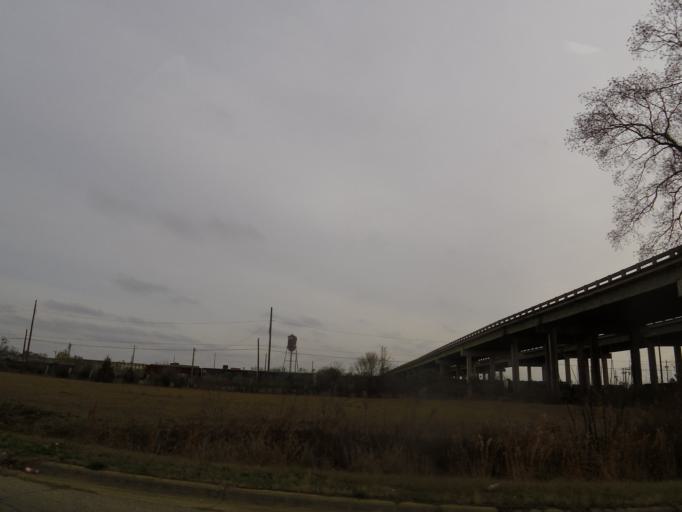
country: US
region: Alabama
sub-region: Montgomery County
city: Montgomery
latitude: 32.3960
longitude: -86.3166
